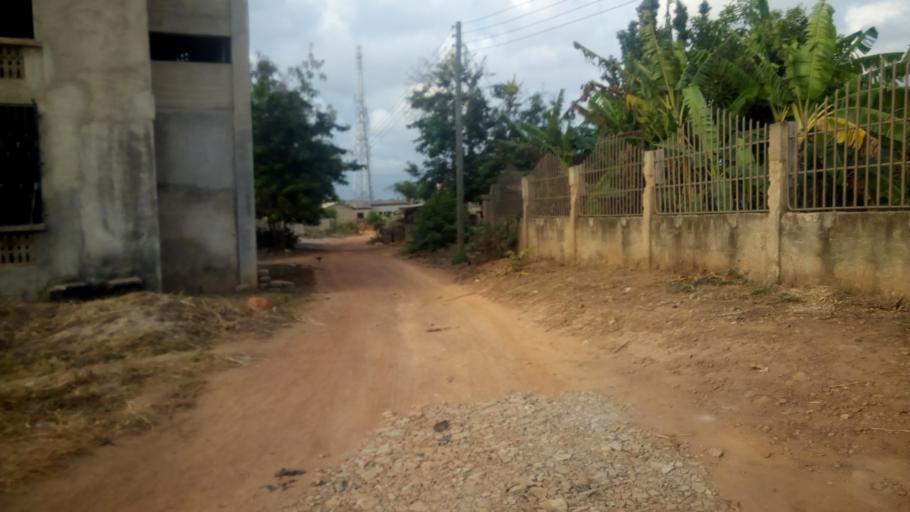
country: GH
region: Central
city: Cape Coast
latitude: 5.1196
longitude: -1.3030
